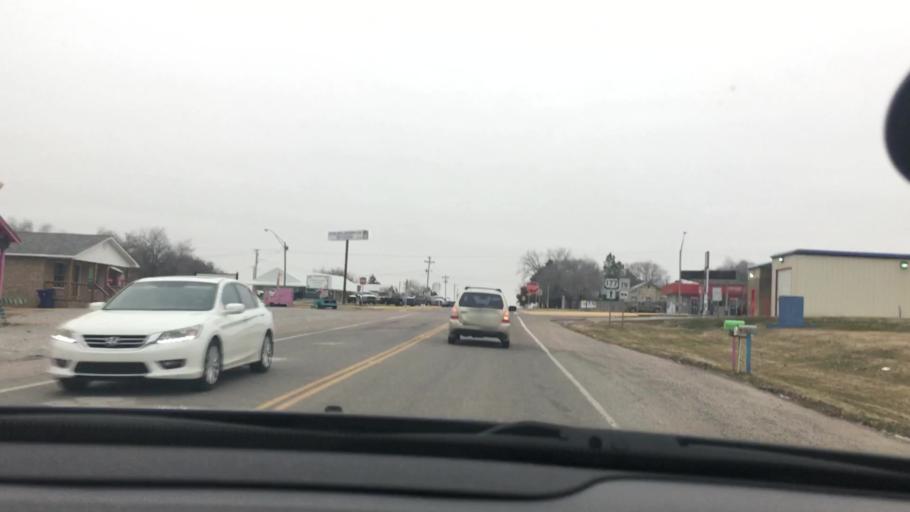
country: US
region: Oklahoma
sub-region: Garvin County
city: Stratford
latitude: 34.7957
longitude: -96.9675
